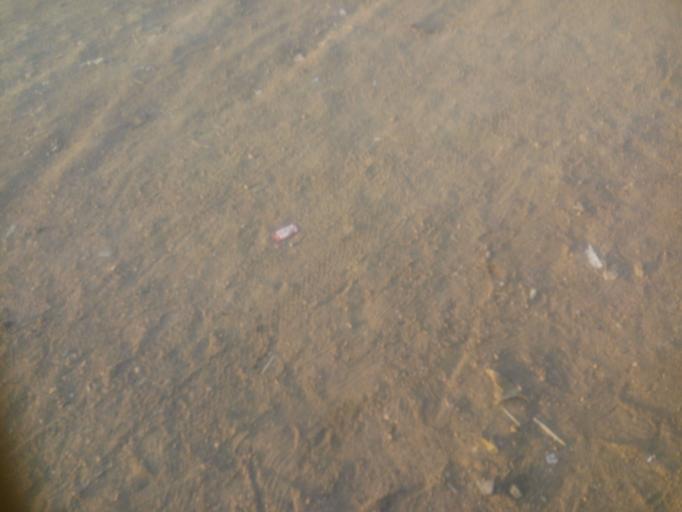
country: IN
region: Maharashtra
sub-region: Nagpur Division
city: Kamthi
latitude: 21.2147
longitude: 79.1885
